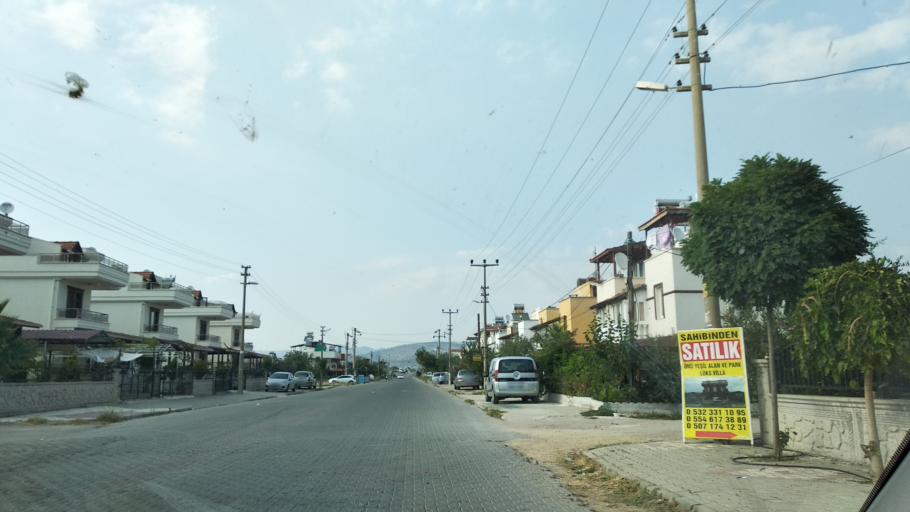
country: TR
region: Izmir
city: Dikili
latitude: 39.1009
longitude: 26.8828
